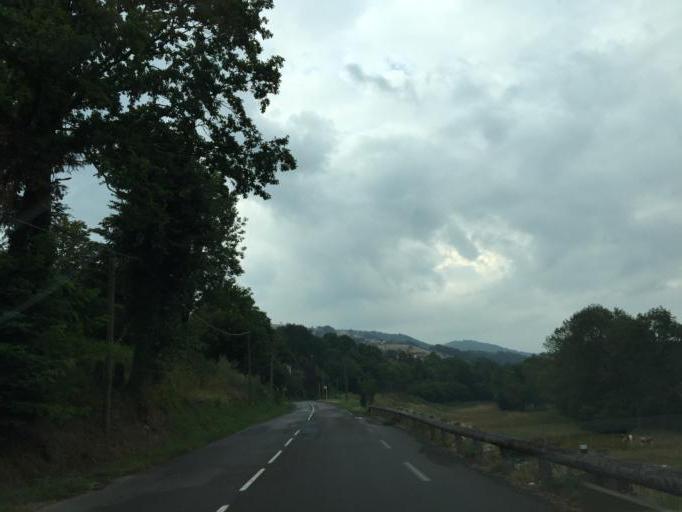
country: FR
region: Rhone-Alpes
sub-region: Departement de la Loire
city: Sorbiers
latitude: 45.5133
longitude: 4.4424
